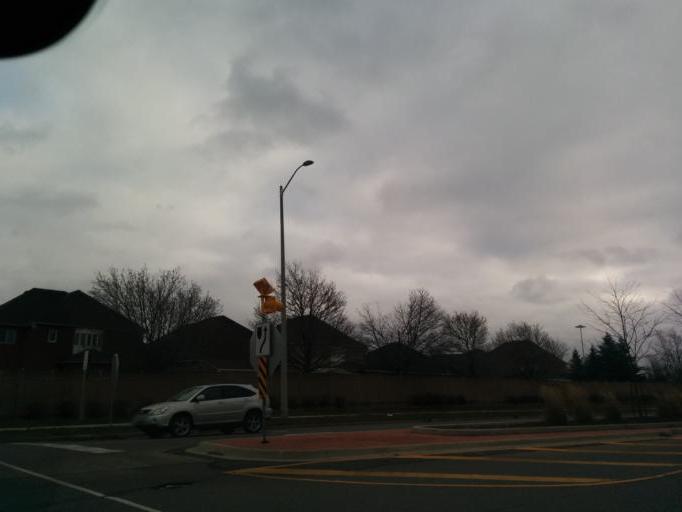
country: CA
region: Ontario
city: Brampton
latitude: 43.7440
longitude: -79.8322
